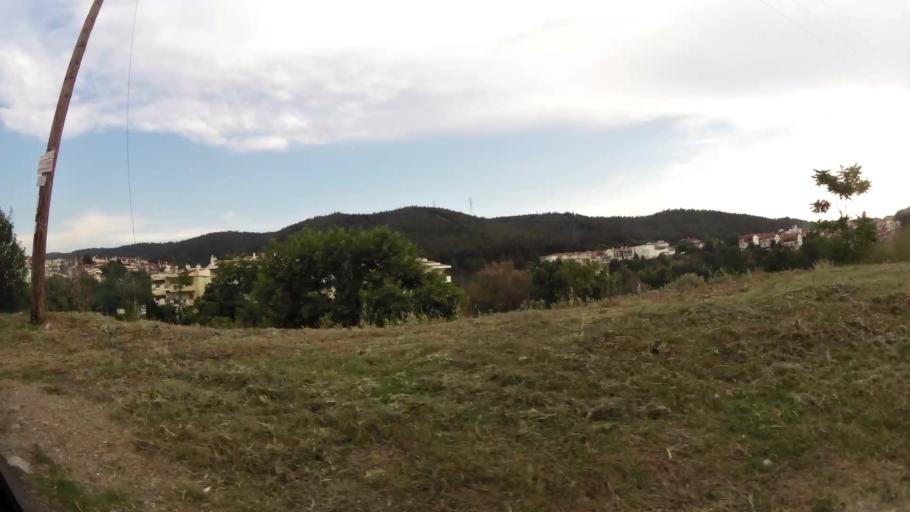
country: GR
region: Central Macedonia
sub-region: Nomos Thessalonikis
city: Pefka
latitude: 40.6617
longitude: 22.9783
